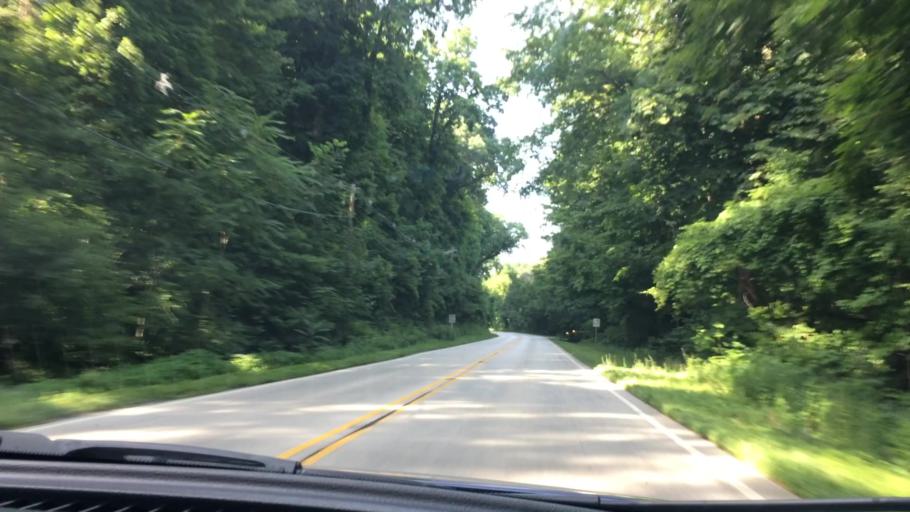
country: US
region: Indiana
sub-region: Tippecanoe County
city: Battle Ground
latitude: 40.4747
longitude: -86.8839
